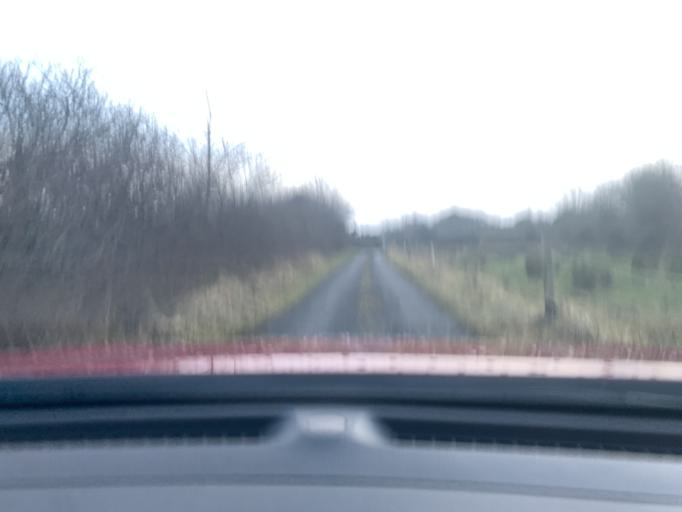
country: IE
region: Connaught
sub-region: Sligo
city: Ballymote
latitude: 53.9891
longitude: -8.4396
